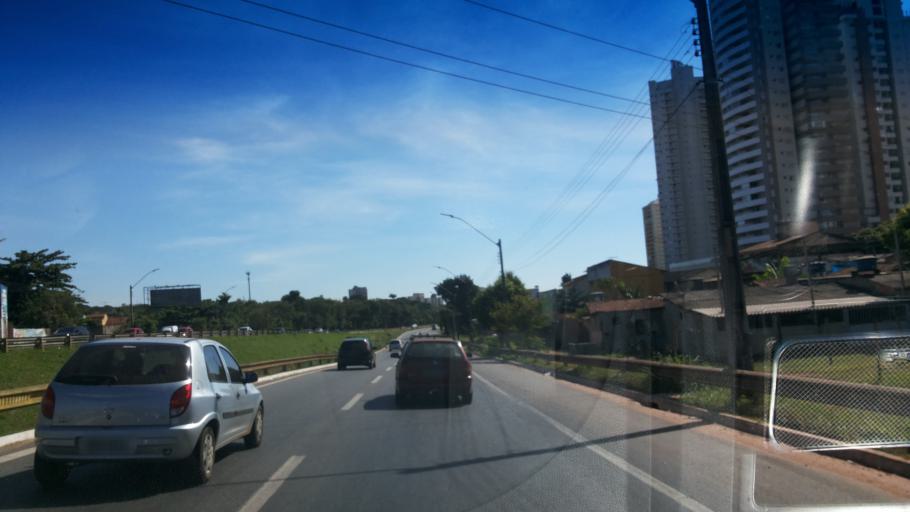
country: BR
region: Goias
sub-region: Goiania
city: Goiania
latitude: -16.7019
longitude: -49.2441
